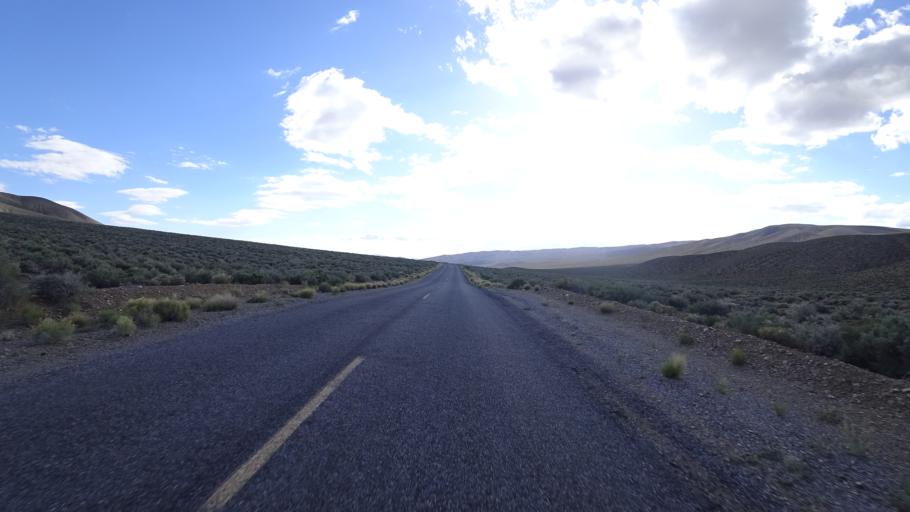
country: US
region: California
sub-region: San Bernardino County
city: Searles Valley
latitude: 36.3342
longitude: -117.1433
